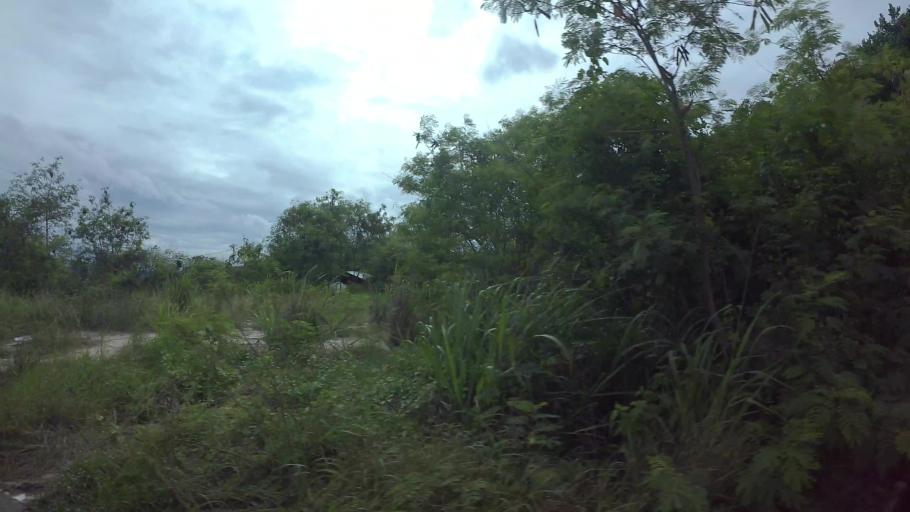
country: TH
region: Chon Buri
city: Sattahip
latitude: 12.7101
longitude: 100.9018
